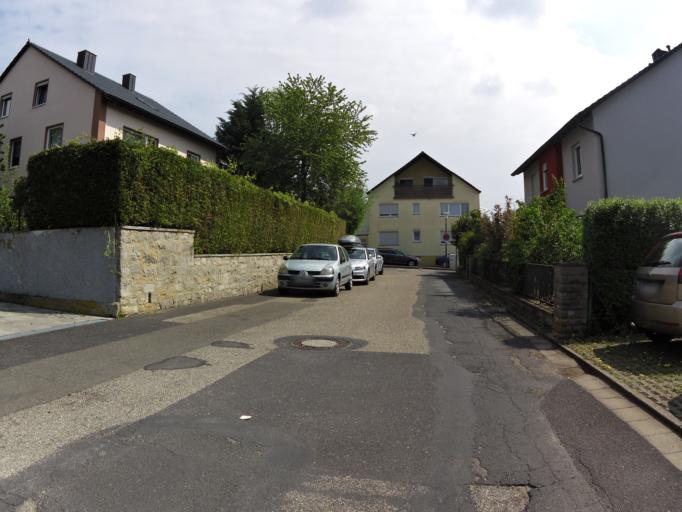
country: DE
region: Bavaria
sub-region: Regierungsbezirk Unterfranken
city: Kurnach
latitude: 49.8454
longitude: 10.0330
